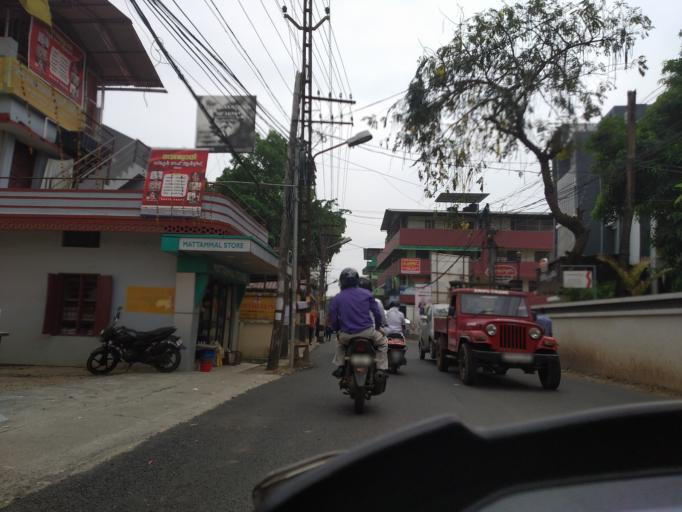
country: IN
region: Kerala
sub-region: Ernakulam
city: Cochin
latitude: 9.9413
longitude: 76.2955
